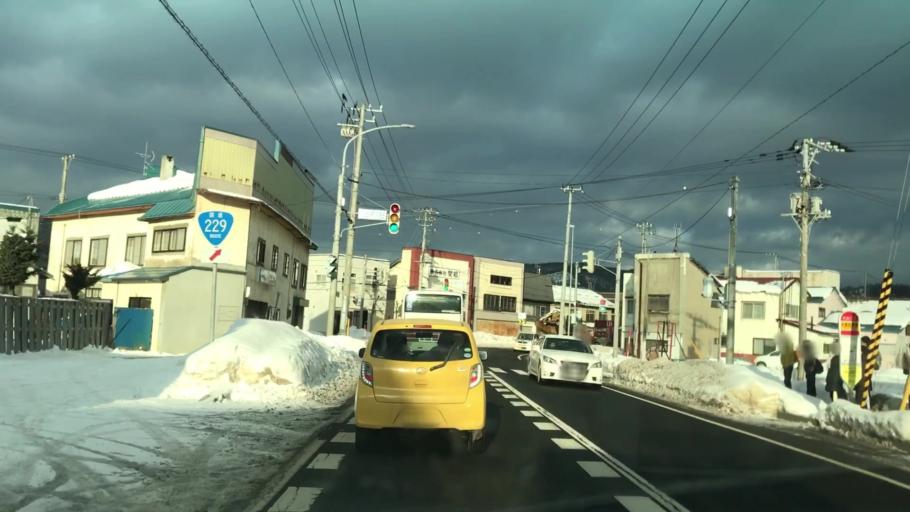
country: JP
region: Hokkaido
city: Yoichi
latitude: 43.2033
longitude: 140.7722
